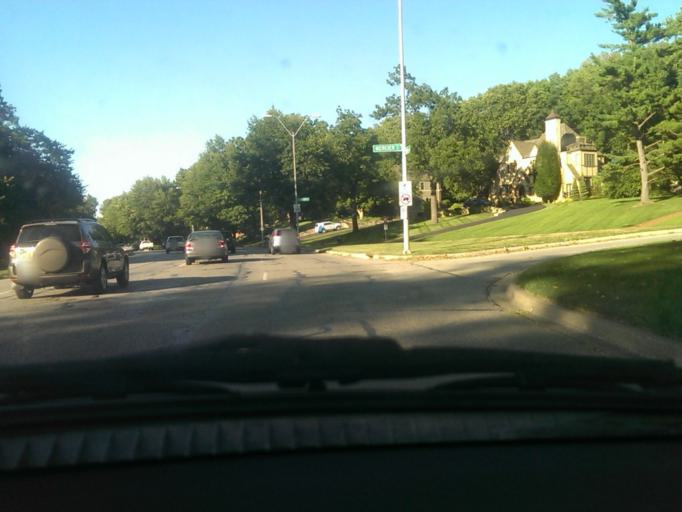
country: US
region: Kansas
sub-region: Johnson County
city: Westwood
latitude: 39.0335
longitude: -94.6030
